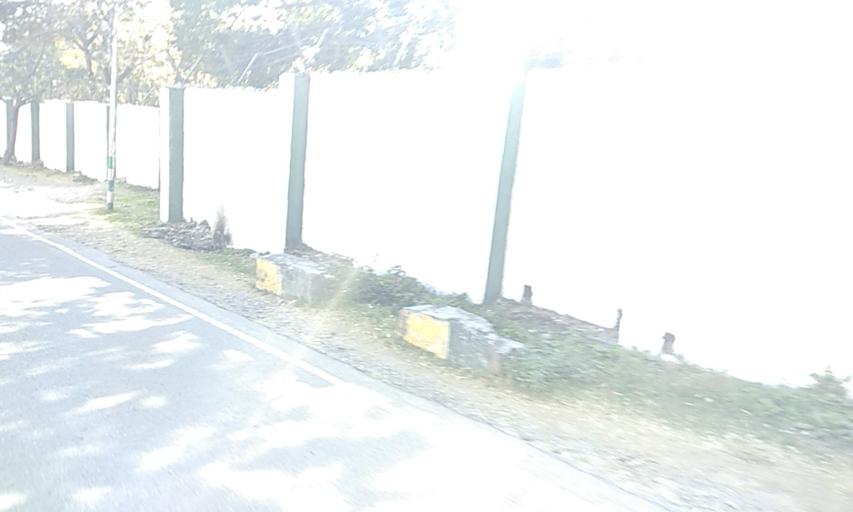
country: IN
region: Himachal Pradesh
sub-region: Kangra
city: Dharmsala
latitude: 32.1780
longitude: 76.3794
